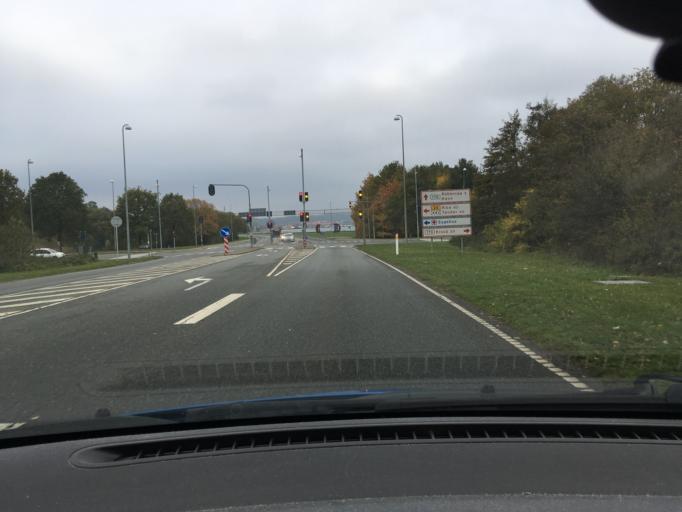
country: DK
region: South Denmark
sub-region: Aabenraa Kommune
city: Aabenraa
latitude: 55.0220
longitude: 9.4260
